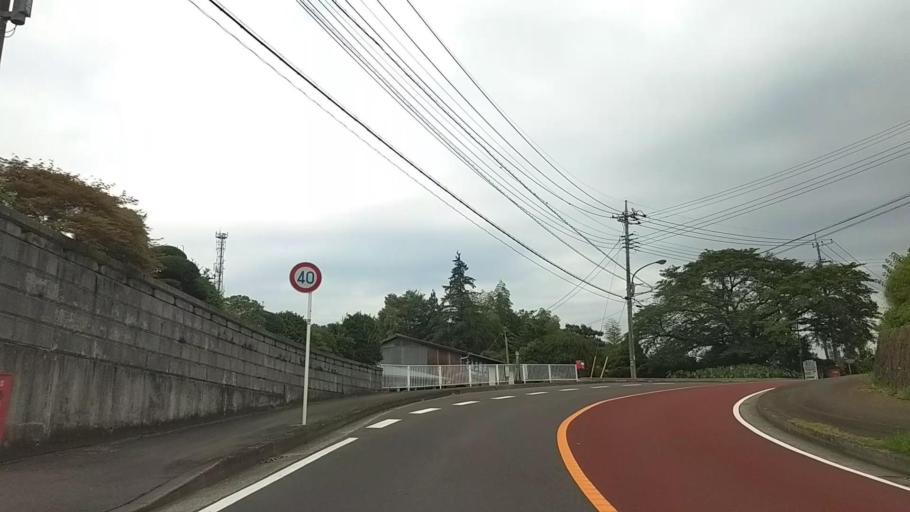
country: JP
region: Kanagawa
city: Hadano
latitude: 35.3400
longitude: 139.1766
